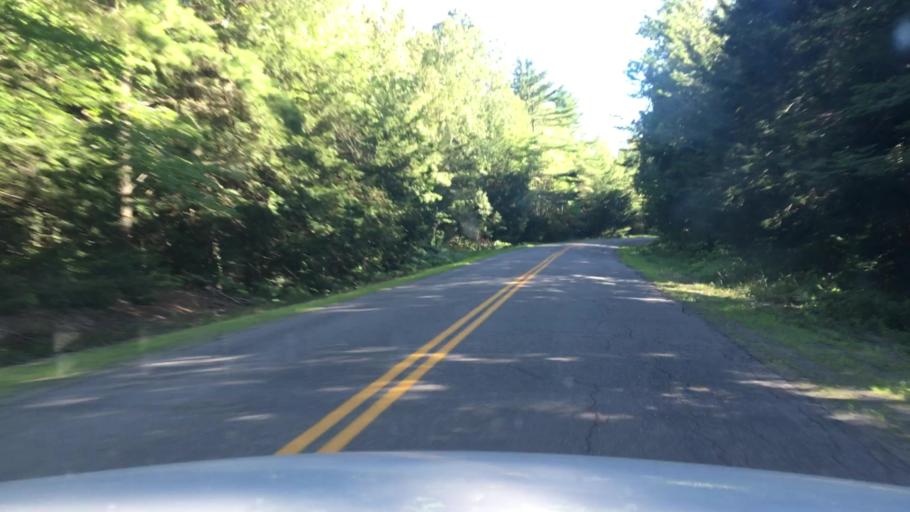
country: US
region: Maine
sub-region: Penobscot County
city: Enfield
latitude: 45.2216
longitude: -68.5805
